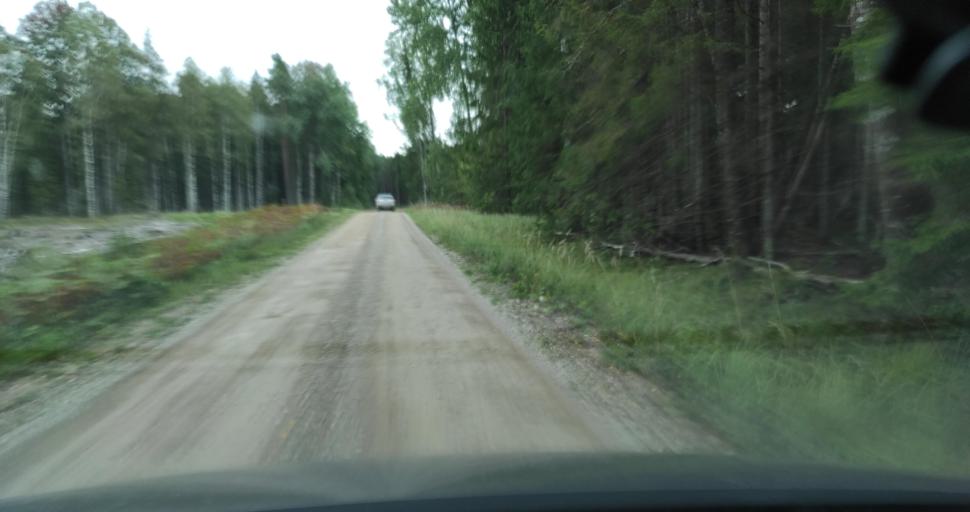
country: LV
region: Talsu Rajons
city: Stende
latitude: 57.0280
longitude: 22.3377
